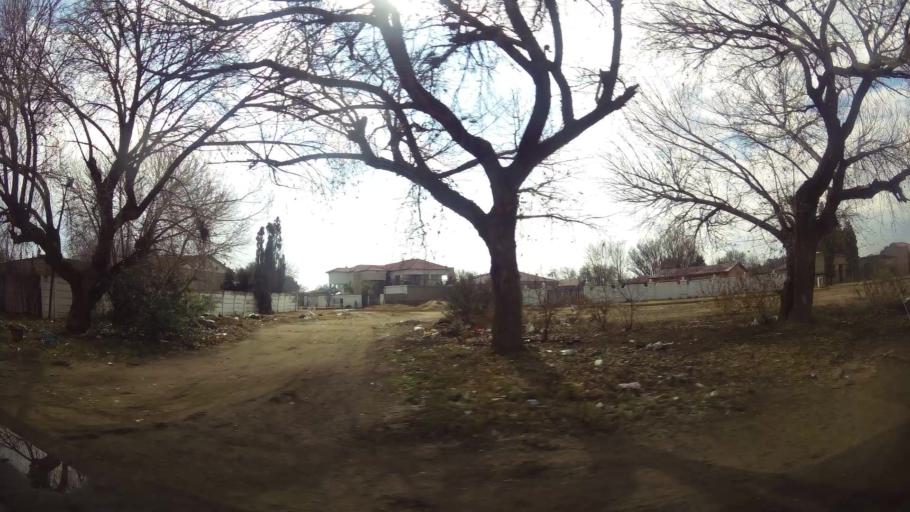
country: ZA
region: Gauteng
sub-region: Sedibeng District Municipality
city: Vereeniging
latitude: -26.6667
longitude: 27.9180
